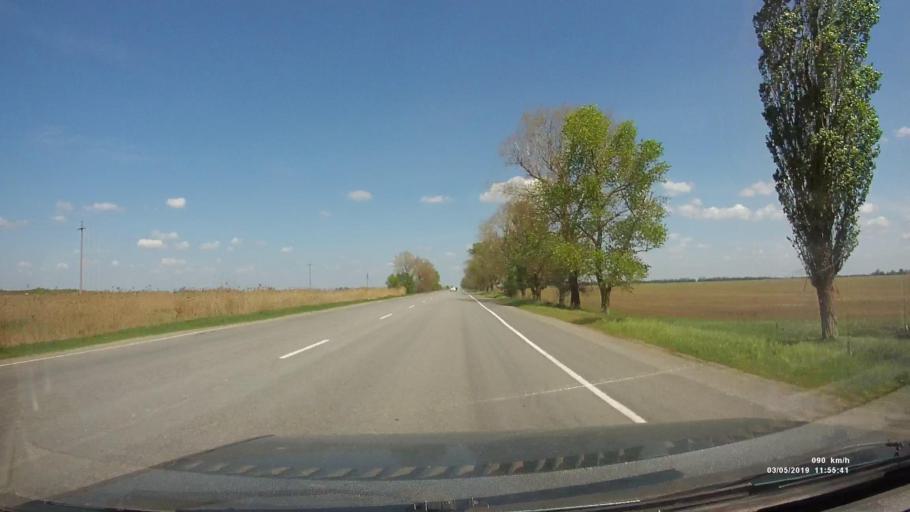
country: RU
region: Rostov
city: Bagayevskaya
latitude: 47.1844
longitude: 40.2936
